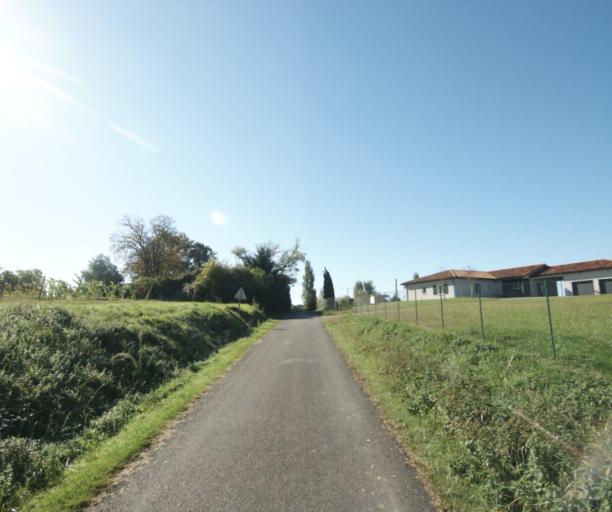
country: FR
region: Midi-Pyrenees
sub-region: Departement du Gers
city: Eauze
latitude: 43.8083
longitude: 0.1685
